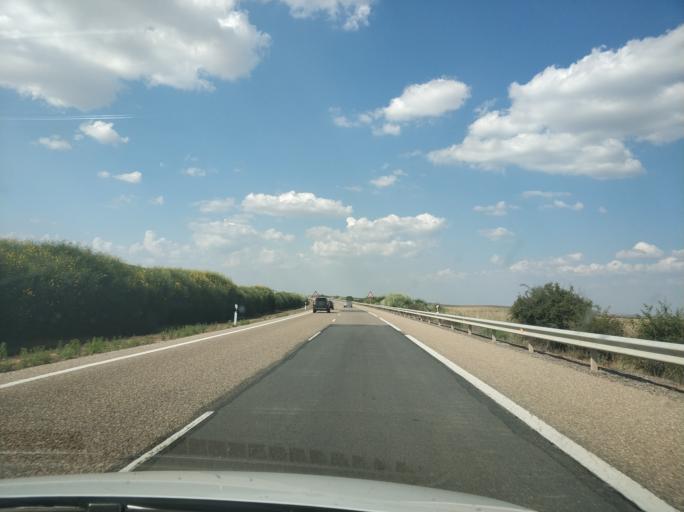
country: ES
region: Castille and Leon
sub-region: Provincia de Zamora
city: Matilla de Arzon
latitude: 42.0778
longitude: -5.6564
